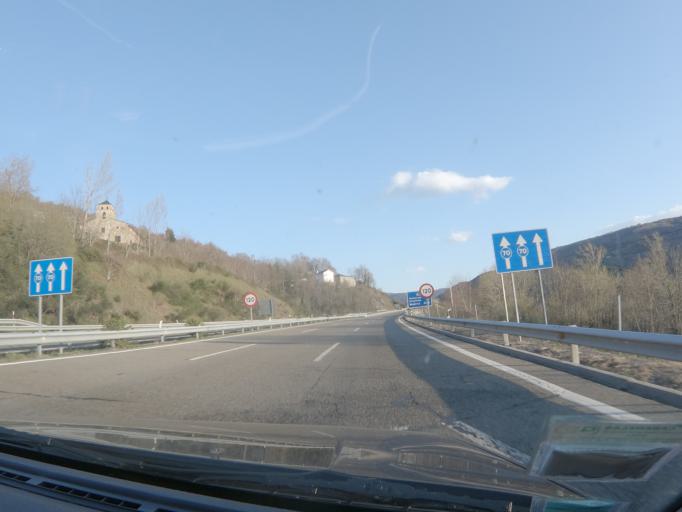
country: ES
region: Galicia
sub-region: Provincia de Lugo
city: San Roman
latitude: 42.7609
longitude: -7.0774
